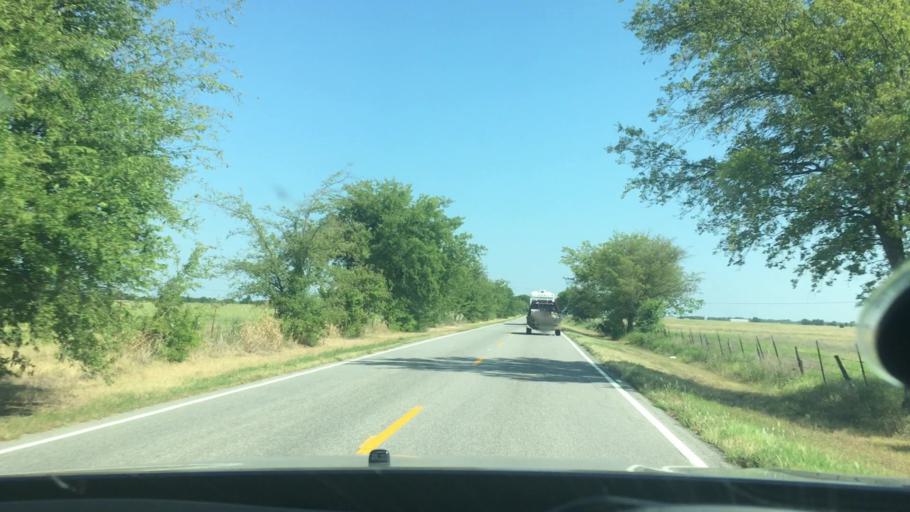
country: US
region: Oklahoma
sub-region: Johnston County
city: Tishomingo
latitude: 34.1600
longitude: -96.5075
